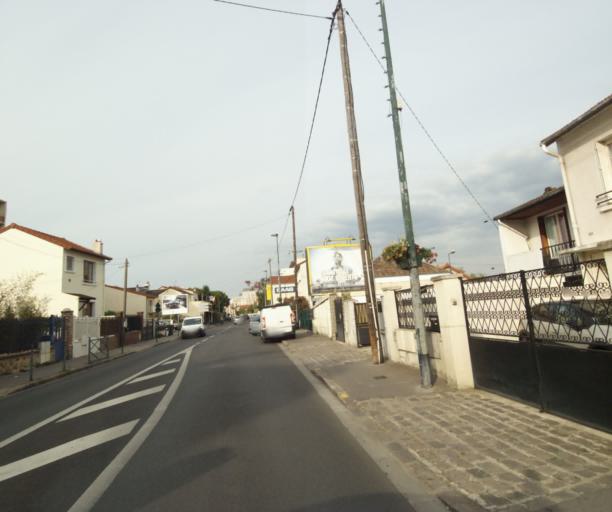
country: FR
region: Ile-de-France
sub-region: Departement des Hauts-de-Seine
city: Asnieres-sur-Seine
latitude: 48.9131
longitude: 2.2879
